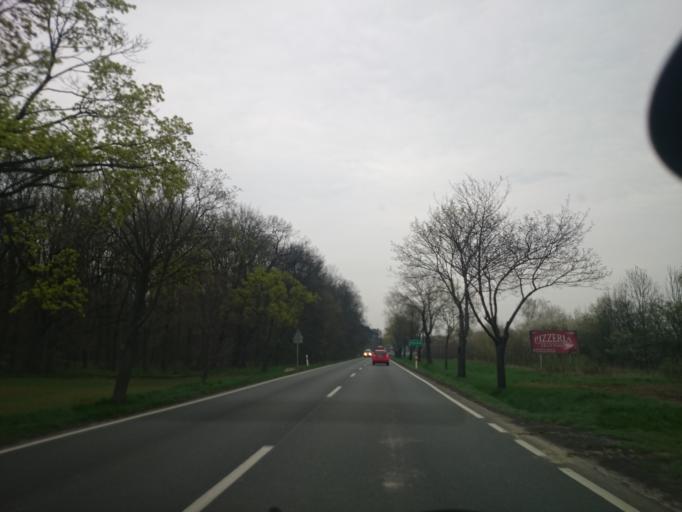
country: PL
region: Opole Voivodeship
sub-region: Powiat nyski
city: Otmuchow
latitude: 50.4560
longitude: 17.1599
